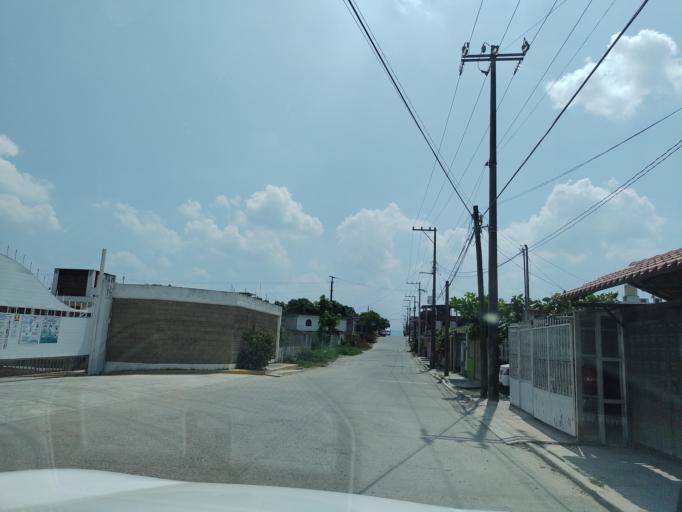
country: MX
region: Veracruz
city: Martinez de la Torre
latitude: 20.0775
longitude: -97.0467
